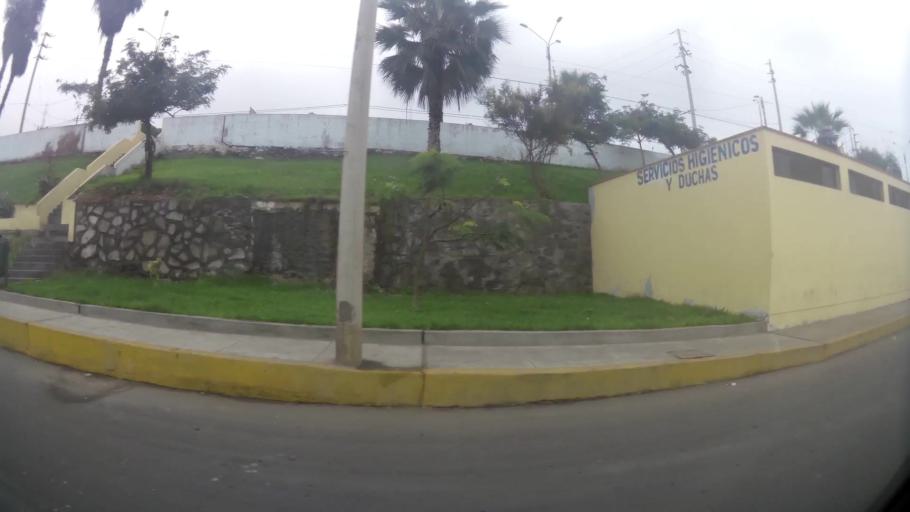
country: PE
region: Lima
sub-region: Provincia de Huaral
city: Chancay
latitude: -11.5847
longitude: -77.2712
